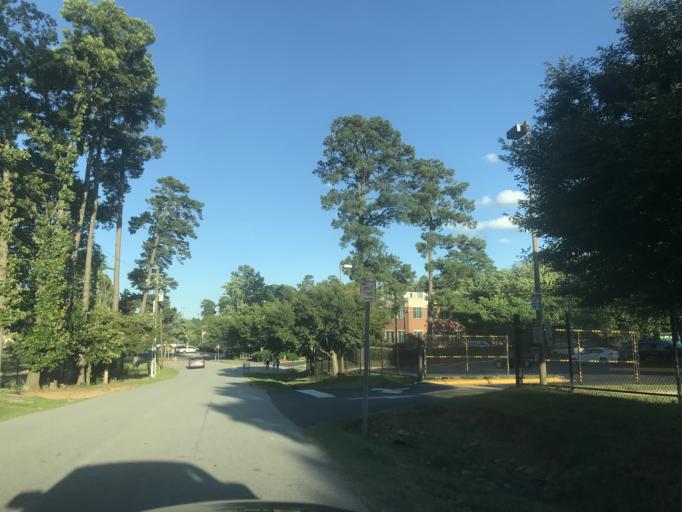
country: US
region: North Carolina
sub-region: Wake County
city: Raleigh
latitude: 35.8373
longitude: -78.6117
